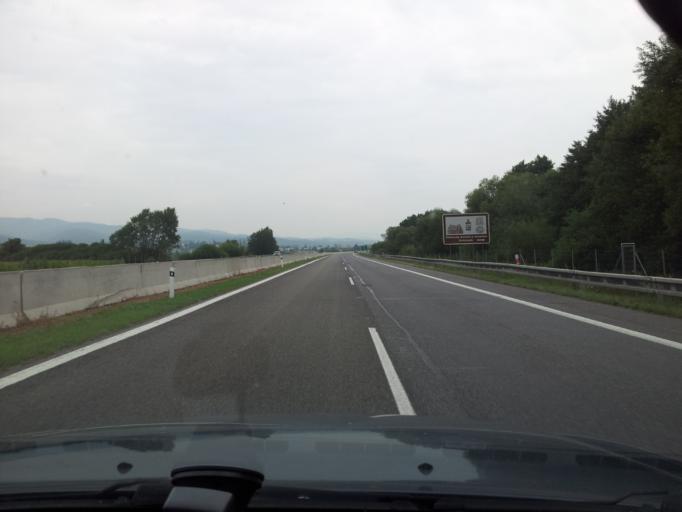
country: SK
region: Banskobystricky
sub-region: Okres Banska Bystrica
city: Zvolen
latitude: 48.6164
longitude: 19.1196
